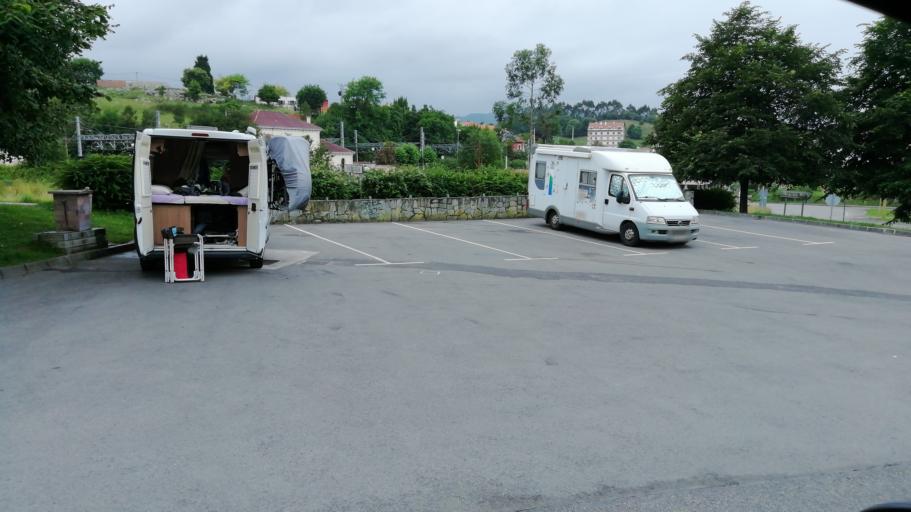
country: ES
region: Asturias
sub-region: Province of Asturias
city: Ribadesella
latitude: 43.4603
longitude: -5.0539
